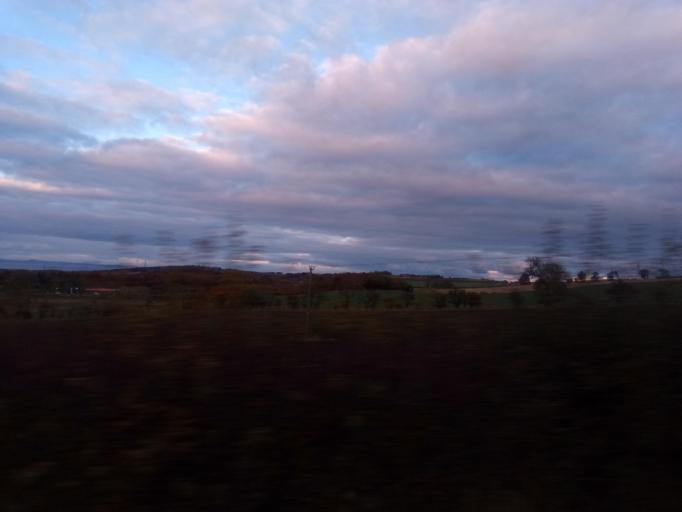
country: GB
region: Scotland
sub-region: Midlothian
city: Dalkeith
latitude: 55.8850
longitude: -3.0274
